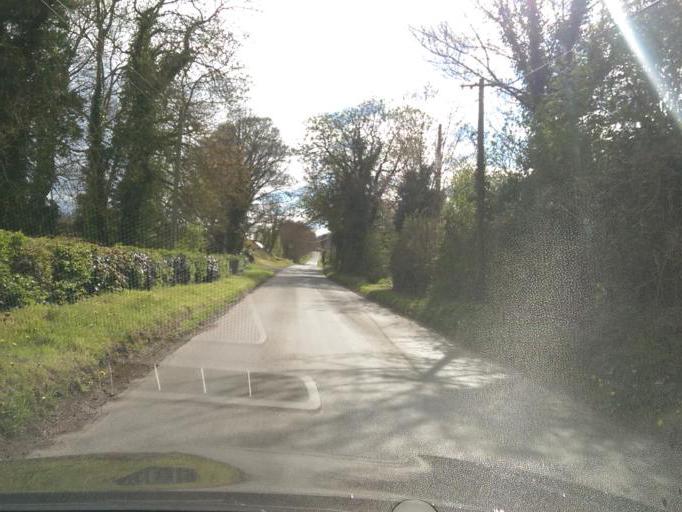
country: IE
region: Leinster
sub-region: Kildare
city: Kilcock
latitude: 53.4995
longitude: -6.6778
